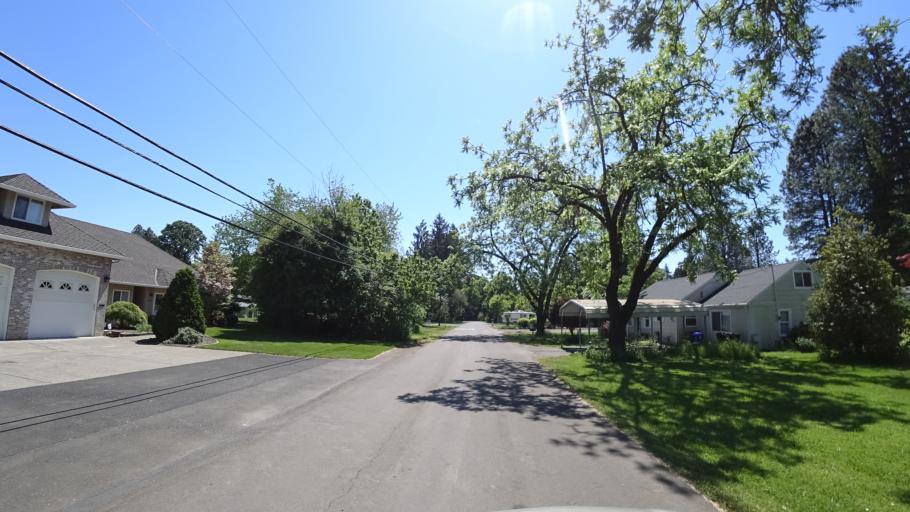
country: US
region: Oregon
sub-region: Washington County
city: Rockcreek
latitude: 45.5262
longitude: -122.9105
